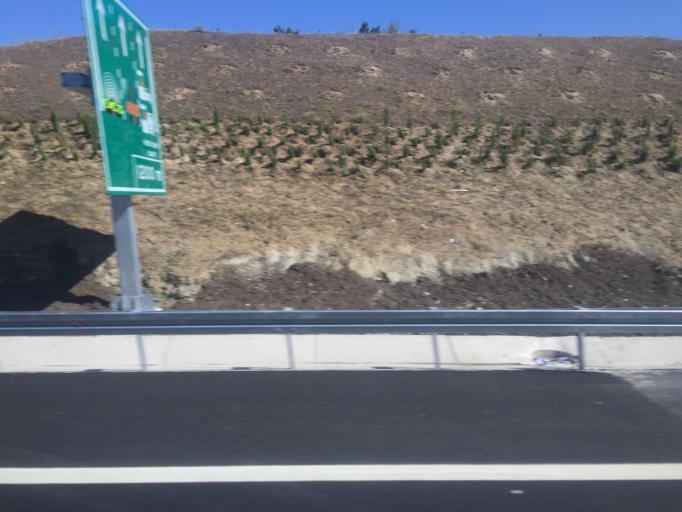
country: TR
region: Bursa
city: Mahmudiye
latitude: 40.2566
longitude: 28.7291
